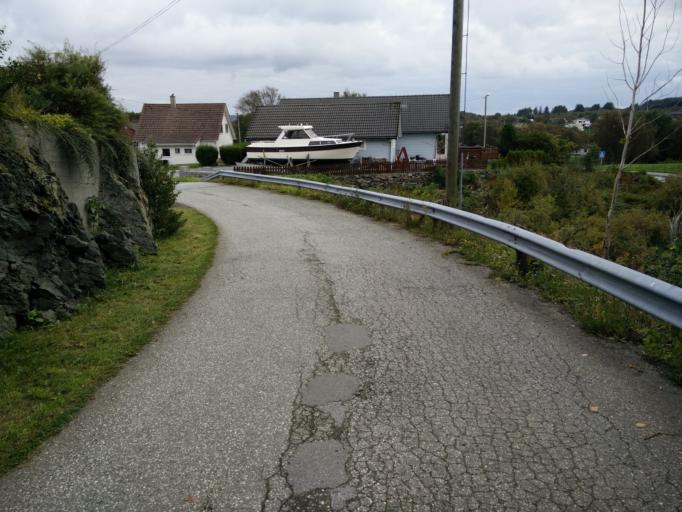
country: NO
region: Hordaland
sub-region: Sveio
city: Sveio
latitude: 59.6056
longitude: 5.2103
